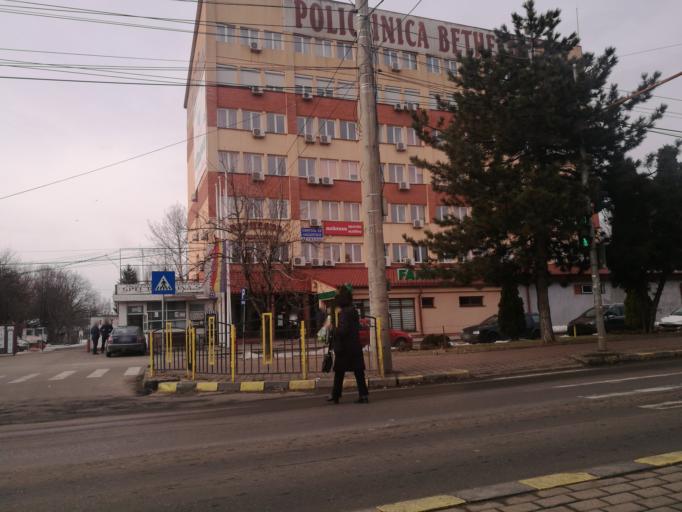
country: RO
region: Suceava
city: Suceava
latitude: 47.6610
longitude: 26.2661
